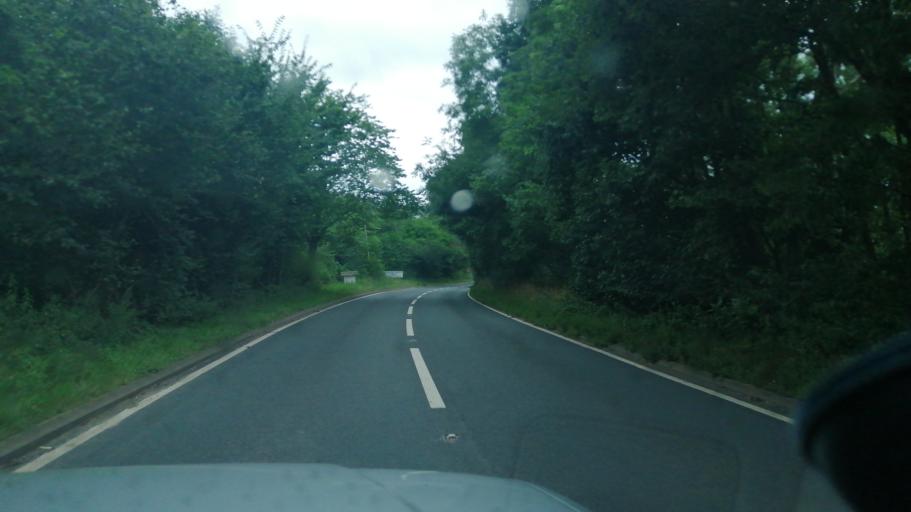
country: GB
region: Wales
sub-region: Monmouthshire
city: Grosmont
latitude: 51.9470
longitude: -2.8720
